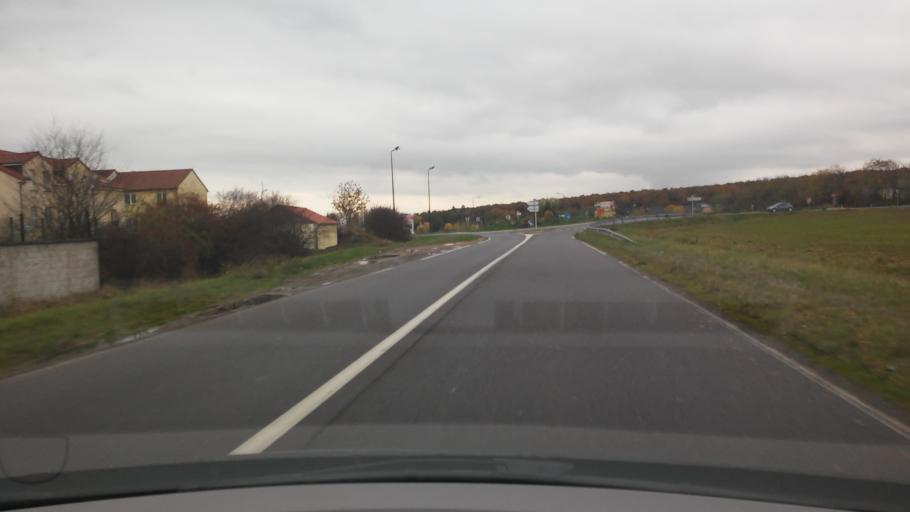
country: FR
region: Lorraine
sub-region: Departement de la Moselle
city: Bousse
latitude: 49.2739
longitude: 6.2014
